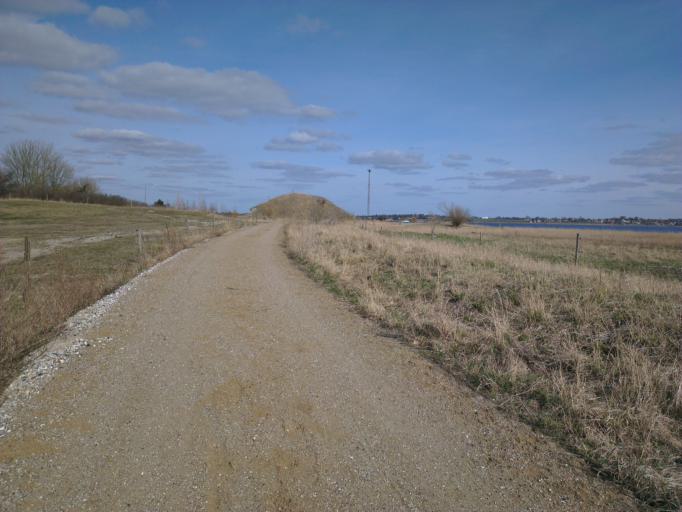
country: DK
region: Zealand
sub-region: Roskilde Kommune
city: Jyllinge
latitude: 55.7504
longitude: 12.0595
